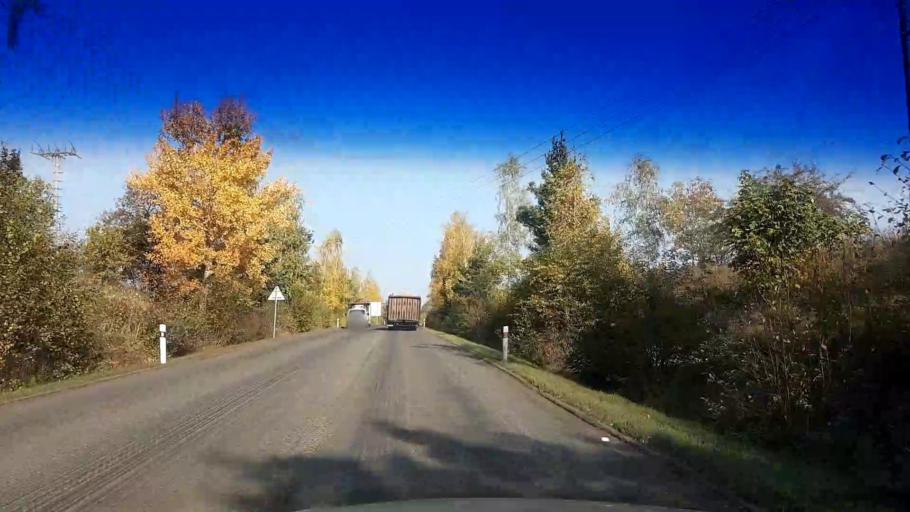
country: CZ
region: Karlovarsky
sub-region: Okres Cheb
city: Cheb
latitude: 50.0761
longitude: 12.3937
